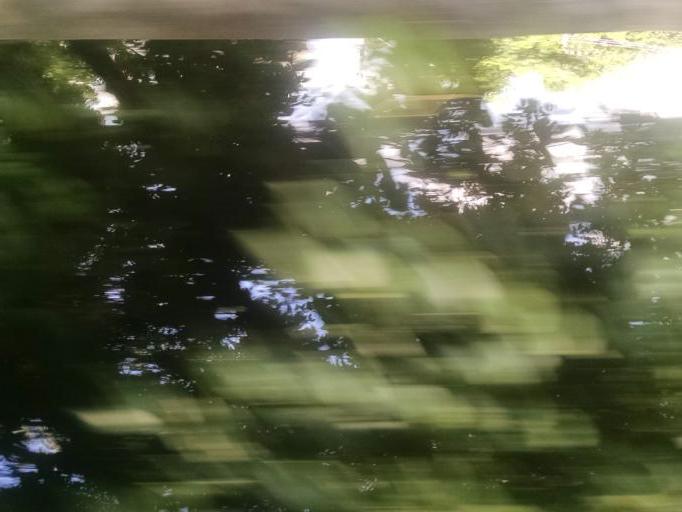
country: BR
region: Rio de Janeiro
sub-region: Rio De Janeiro
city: Rio de Janeiro
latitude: -22.8736
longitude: -43.2867
